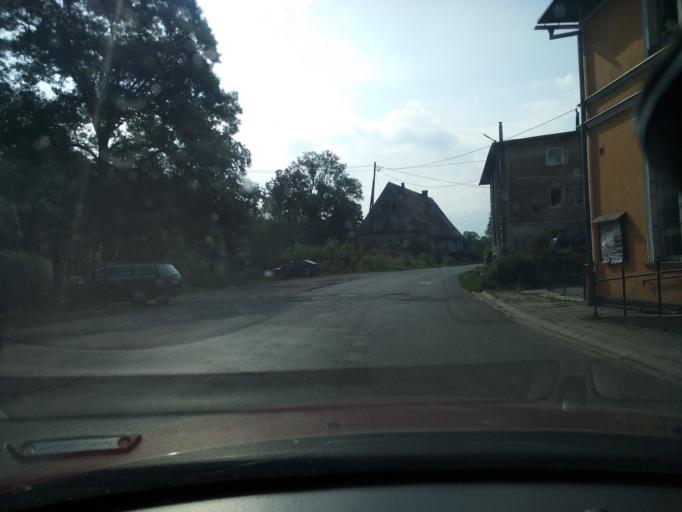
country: PL
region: Lower Silesian Voivodeship
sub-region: Powiat jeleniogorski
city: Stara Kamienica
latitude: 50.9404
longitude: 15.5962
